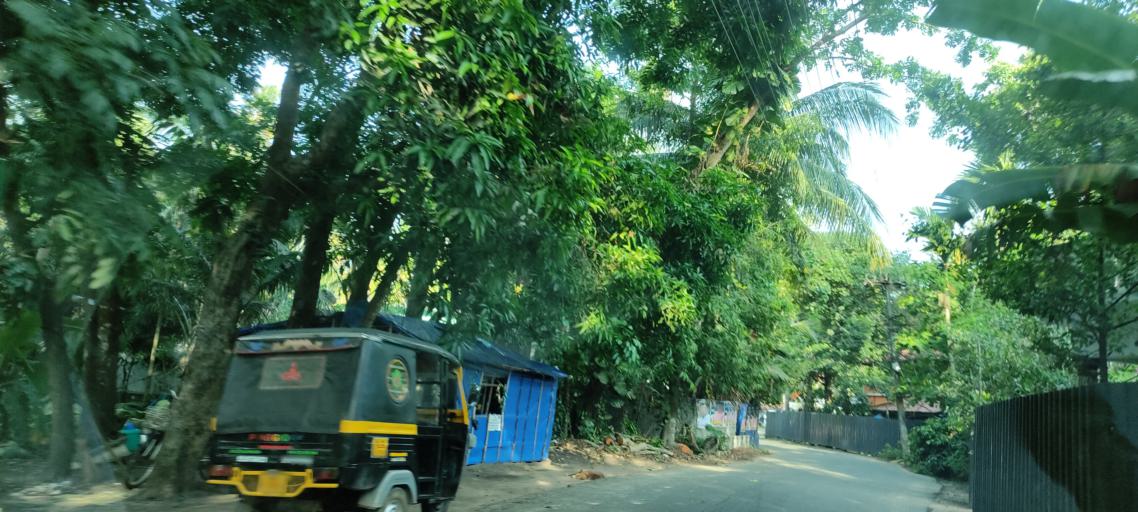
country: IN
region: Kerala
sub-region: Alappuzha
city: Vayalar
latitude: 9.7283
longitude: 76.2948
